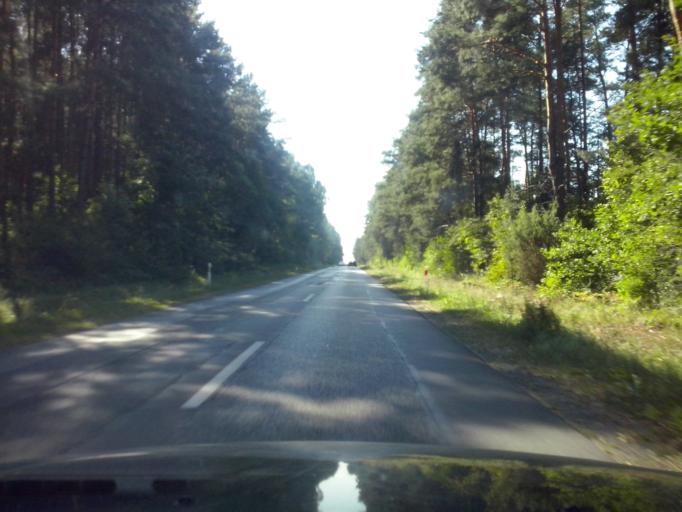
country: PL
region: Swietokrzyskie
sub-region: Powiat kielecki
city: Daleszyce
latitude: 50.8118
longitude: 20.7437
